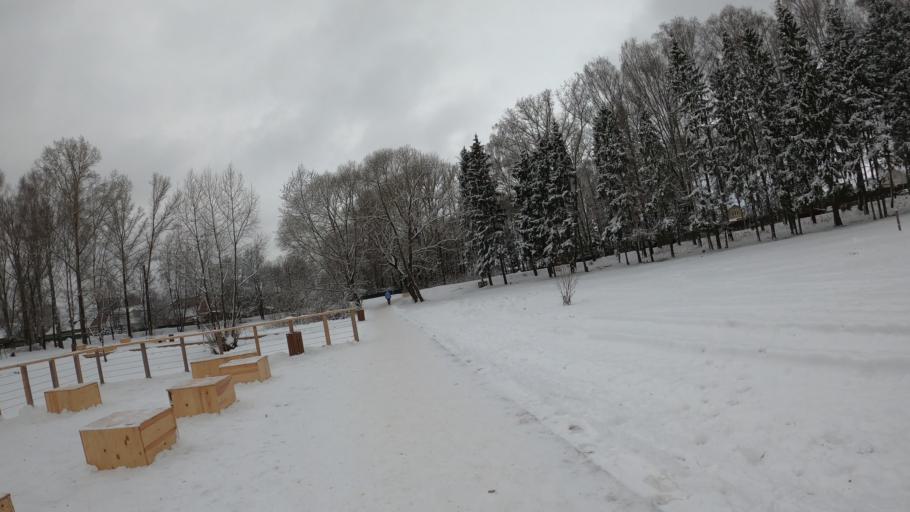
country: RU
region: Jaroslavl
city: Pereslavl'-Zalesskiy
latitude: 56.7514
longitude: 38.8637
